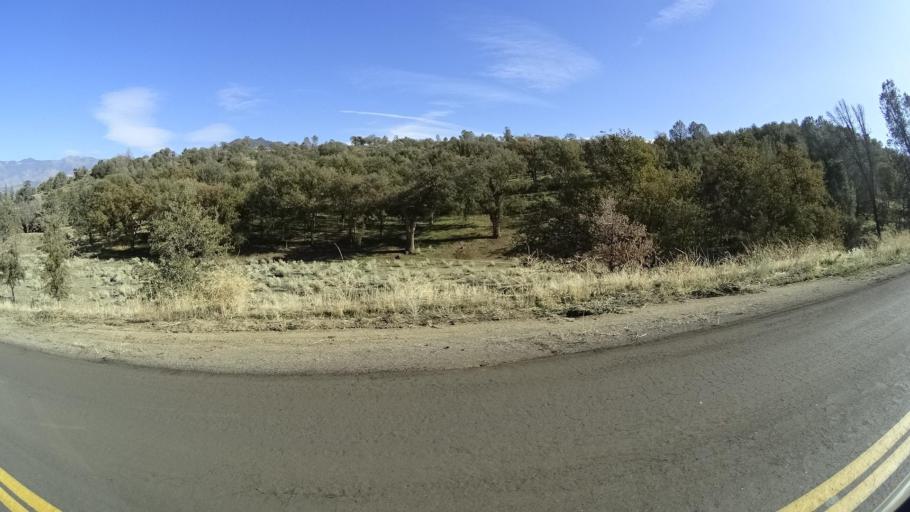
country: US
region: California
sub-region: Kern County
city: Bodfish
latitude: 35.3799
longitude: -118.5568
